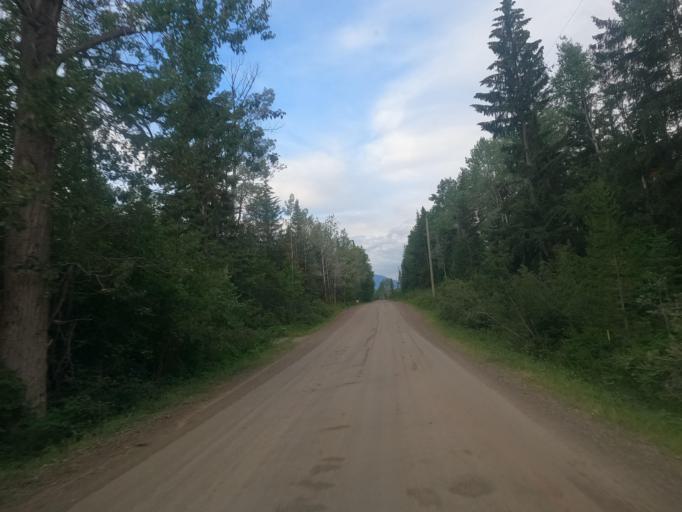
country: CA
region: British Columbia
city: Golden
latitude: 51.4457
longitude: -117.0123
